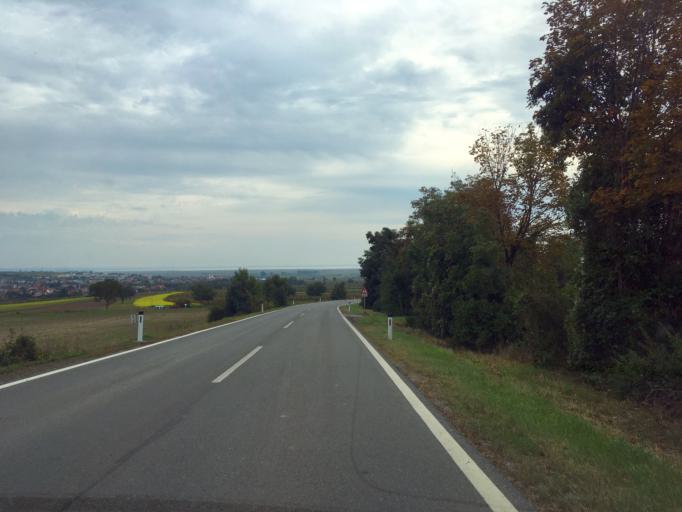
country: AT
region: Burgenland
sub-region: Eisenstadt-Umgebung
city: Breitenbrunn
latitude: 47.9574
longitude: 16.7372
